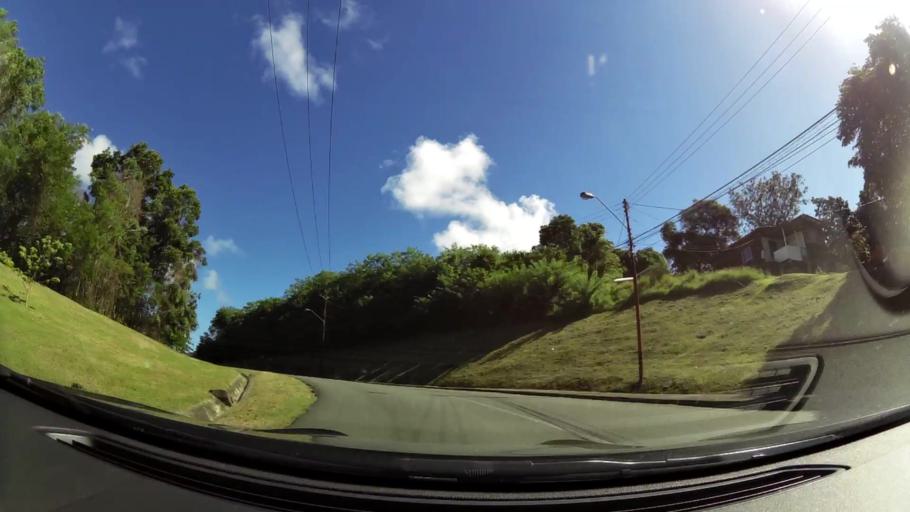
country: TT
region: Tobago
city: Scarborough
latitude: 11.1836
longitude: -60.7320
